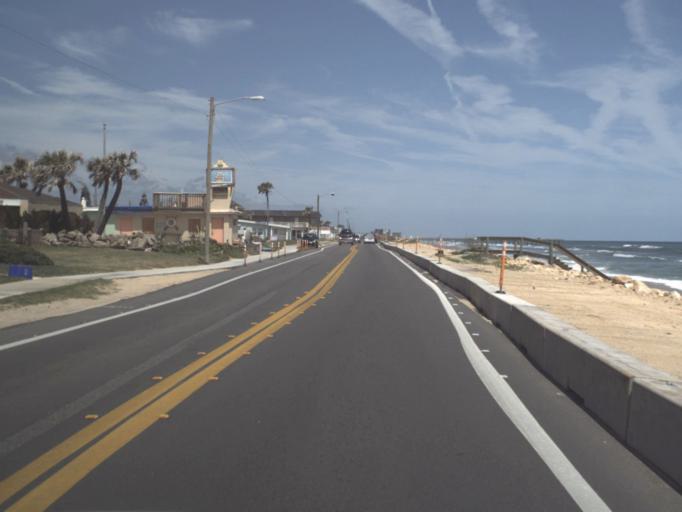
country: US
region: Florida
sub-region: Flagler County
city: Flagler Beach
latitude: 29.4710
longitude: -81.1226
